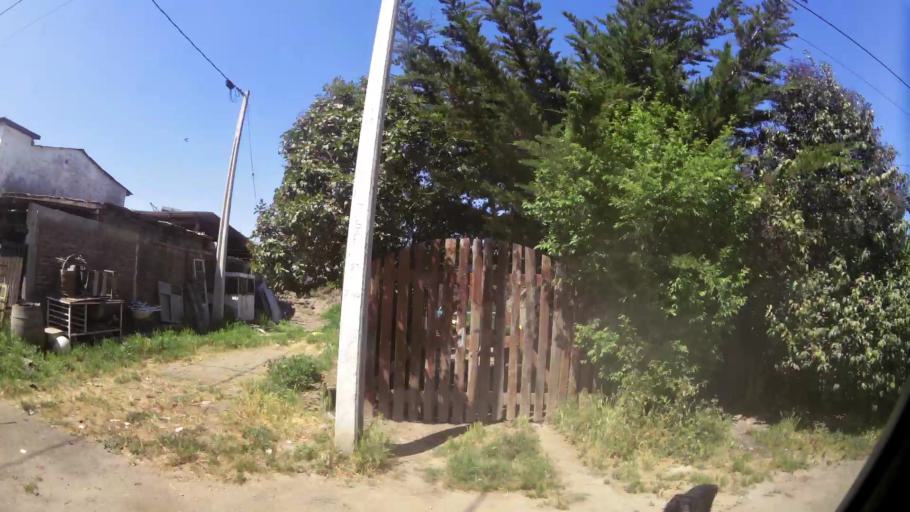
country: CL
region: Santiago Metropolitan
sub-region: Provincia de Talagante
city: Penaflor
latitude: -33.5938
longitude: -70.8088
